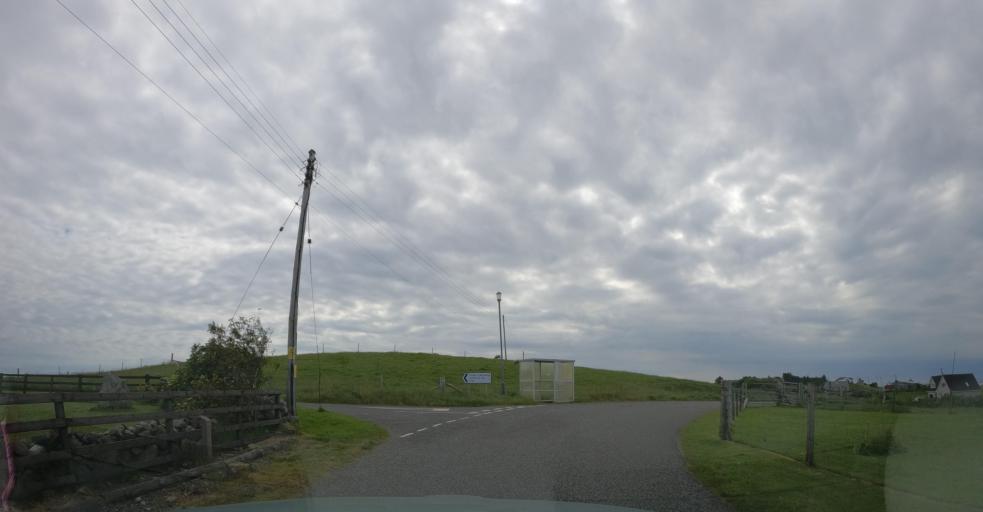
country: GB
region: Scotland
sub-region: Eilean Siar
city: Isle of Lewis
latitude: 58.2725
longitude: -6.3047
